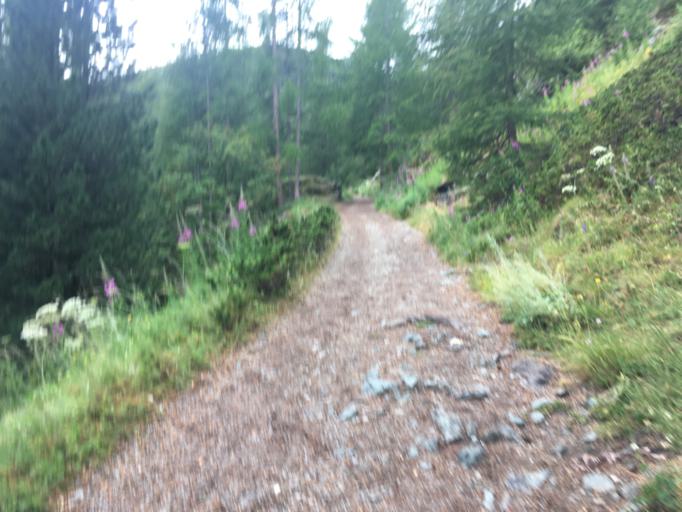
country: CH
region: Valais
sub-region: Visp District
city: Zermatt
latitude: 46.0092
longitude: 7.7308
